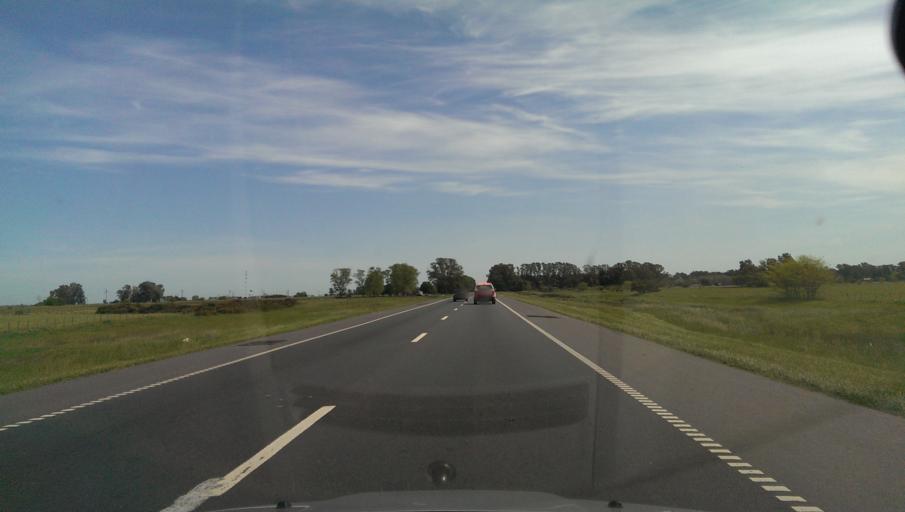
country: AR
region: Buenos Aires
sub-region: Partido de Las Flores
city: Las Flores
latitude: -36.3739
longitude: -59.4739
